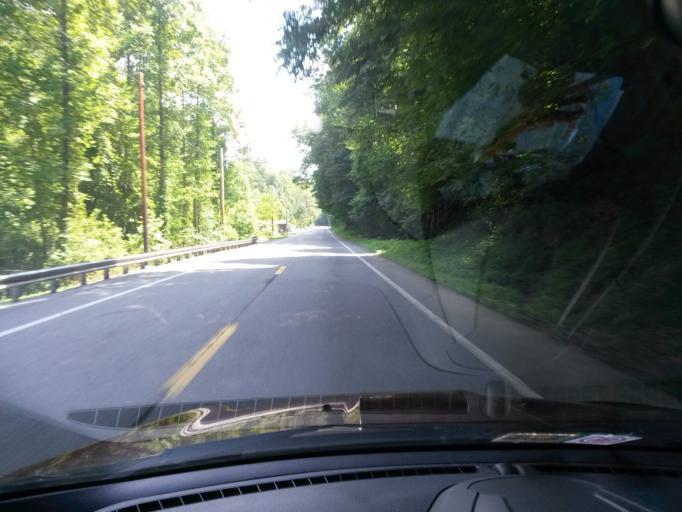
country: US
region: West Virginia
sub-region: Wyoming County
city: Pineville
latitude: 37.5419
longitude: -81.5847
